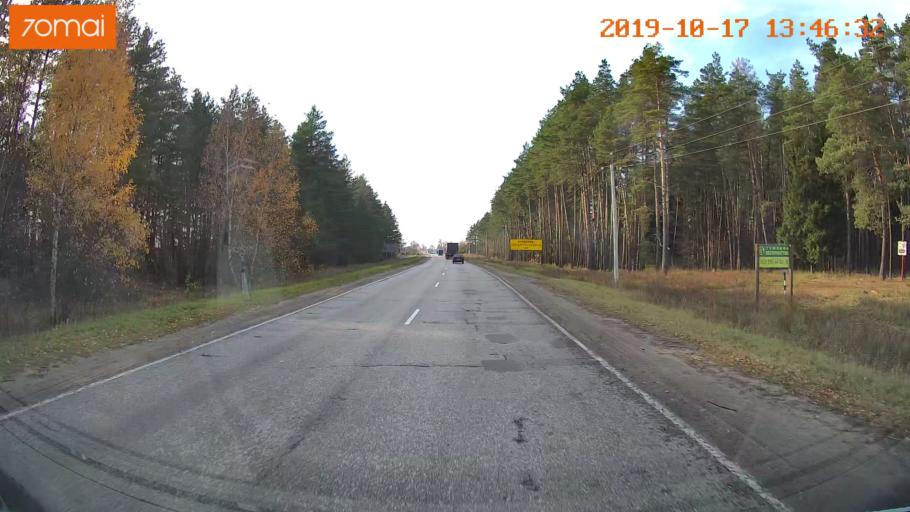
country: RU
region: Rjazan
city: Tuma
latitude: 55.1476
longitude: 40.4871
